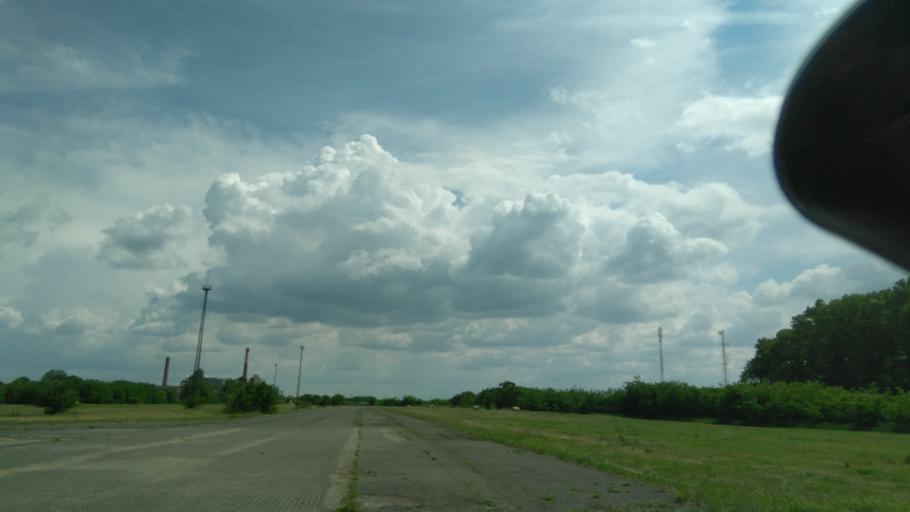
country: HU
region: Bekes
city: Mezohegyes
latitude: 46.3155
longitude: 20.8045
